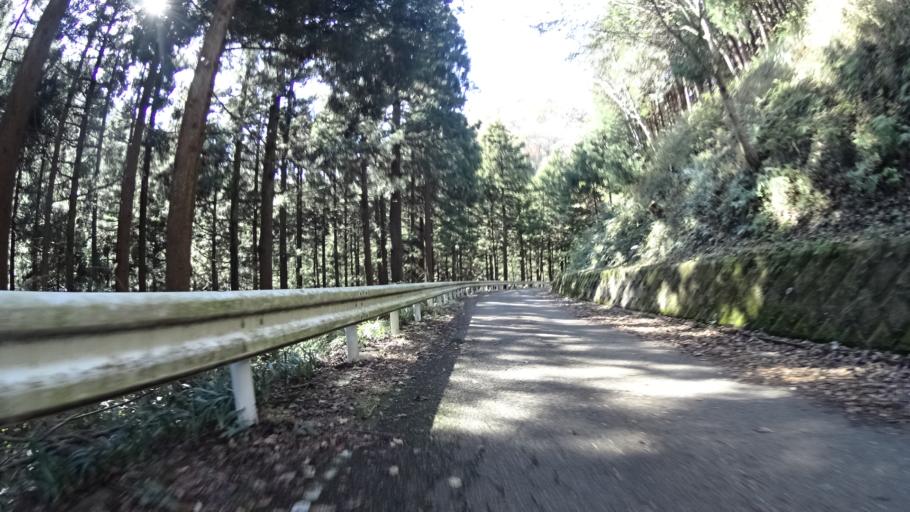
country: JP
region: Kanagawa
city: Atsugi
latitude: 35.5194
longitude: 139.2751
